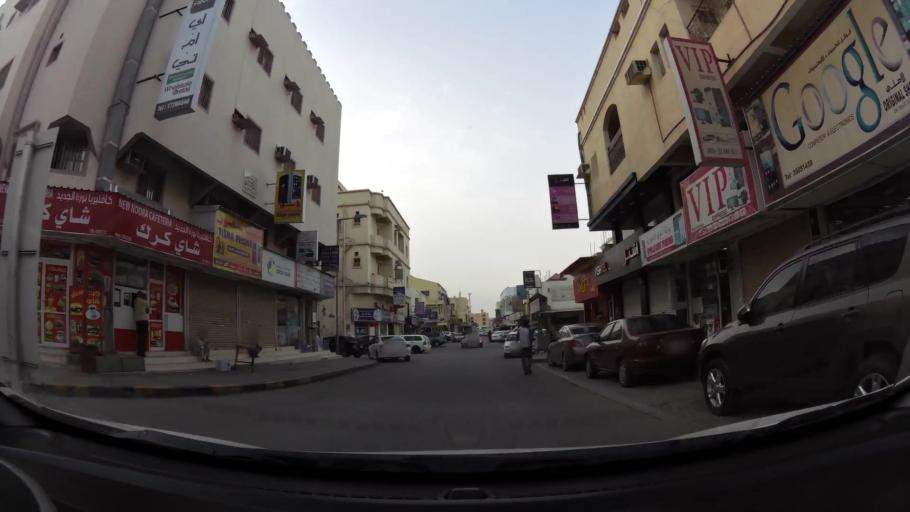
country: BH
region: Northern
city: Ar Rifa'
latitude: 26.1219
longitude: 50.5675
